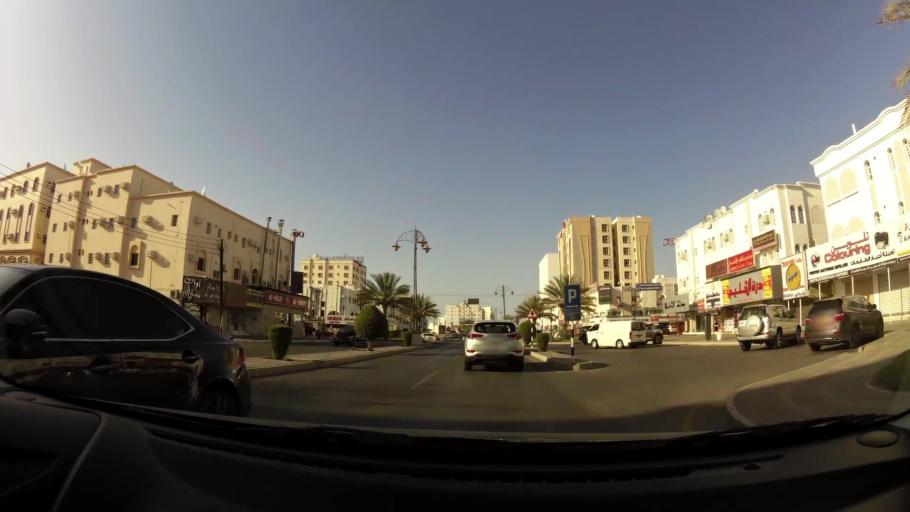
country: OM
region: Muhafazat Masqat
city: As Sib al Jadidah
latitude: 23.6372
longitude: 58.2021
